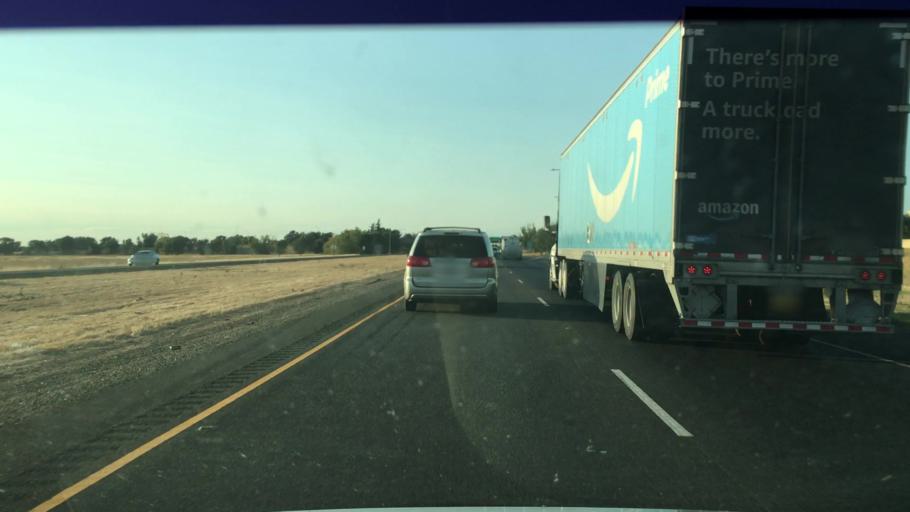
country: US
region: California
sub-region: Sacramento County
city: Laguna
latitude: 38.4044
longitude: -121.4827
